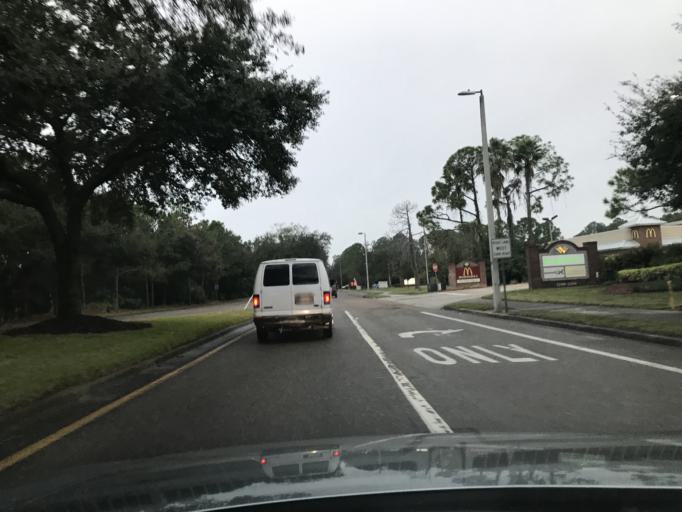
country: US
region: Florida
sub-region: Hillsborough County
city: Westchase
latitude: 28.0558
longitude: -82.6253
